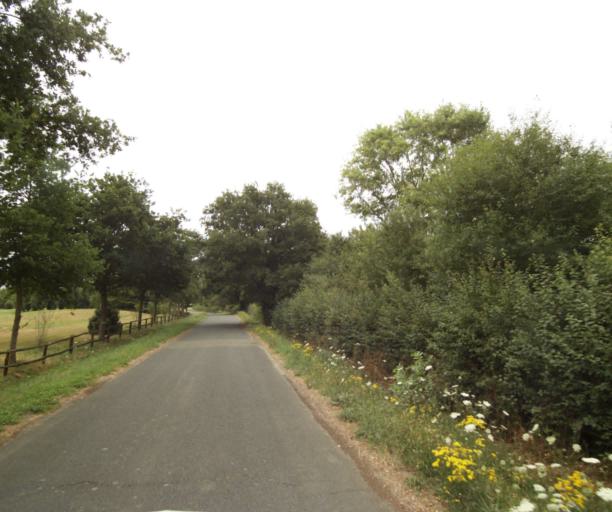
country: FR
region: Pays de la Loire
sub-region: Departement de la Sarthe
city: Sable-sur-Sarthe
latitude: 47.8191
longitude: -0.3616
